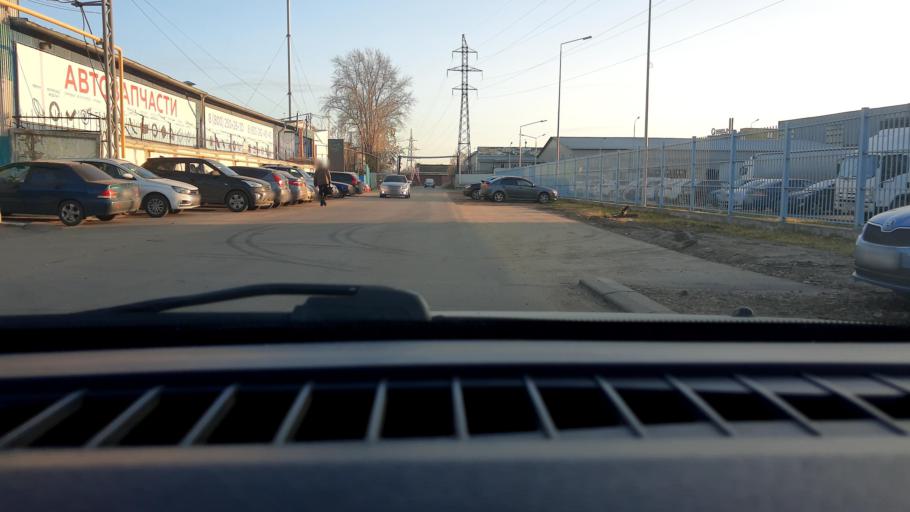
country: RU
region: Nizjnij Novgorod
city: Gorbatovka
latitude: 56.3053
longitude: 43.8662
